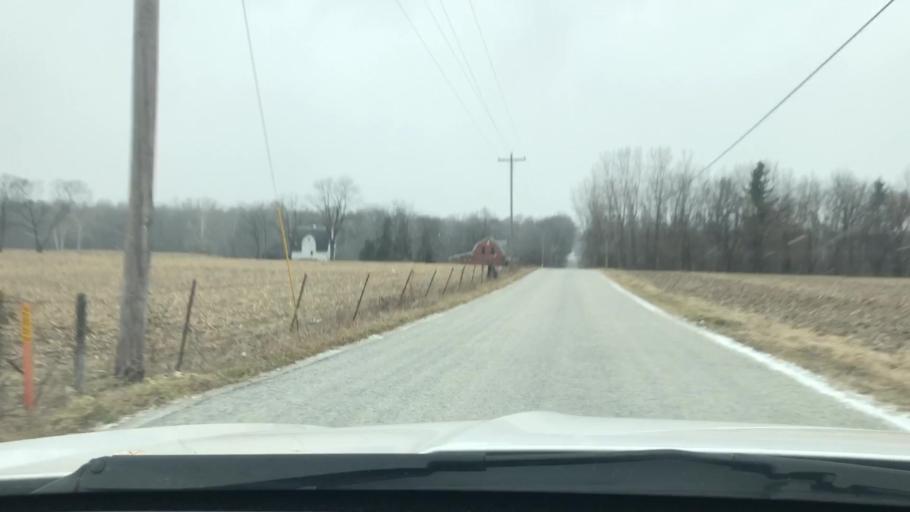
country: US
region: Indiana
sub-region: Fulton County
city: Akron
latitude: 41.0413
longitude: -86.0570
